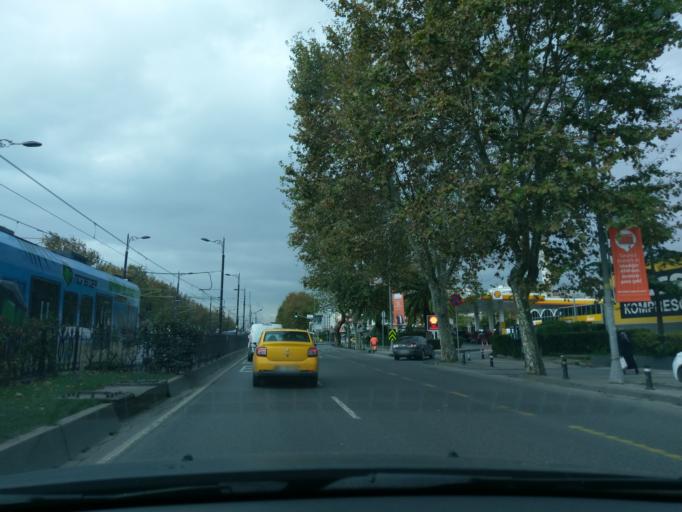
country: TR
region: Istanbul
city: Istanbul
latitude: 41.0175
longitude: 28.9289
